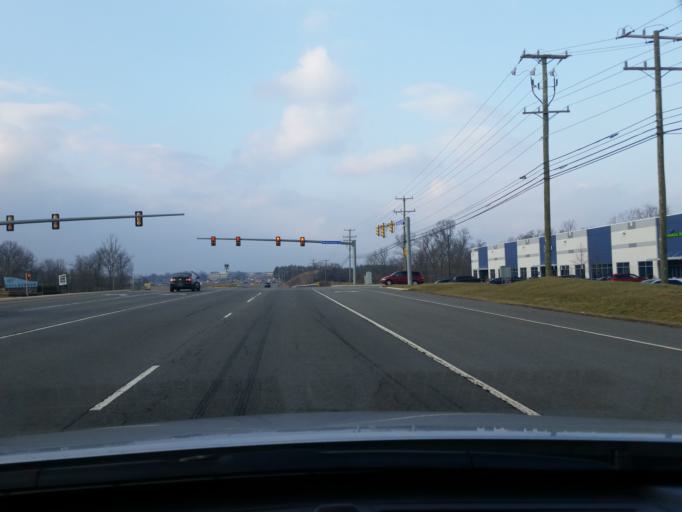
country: US
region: Virginia
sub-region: Loudoun County
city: University Center
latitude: 39.0435
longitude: -77.4500
